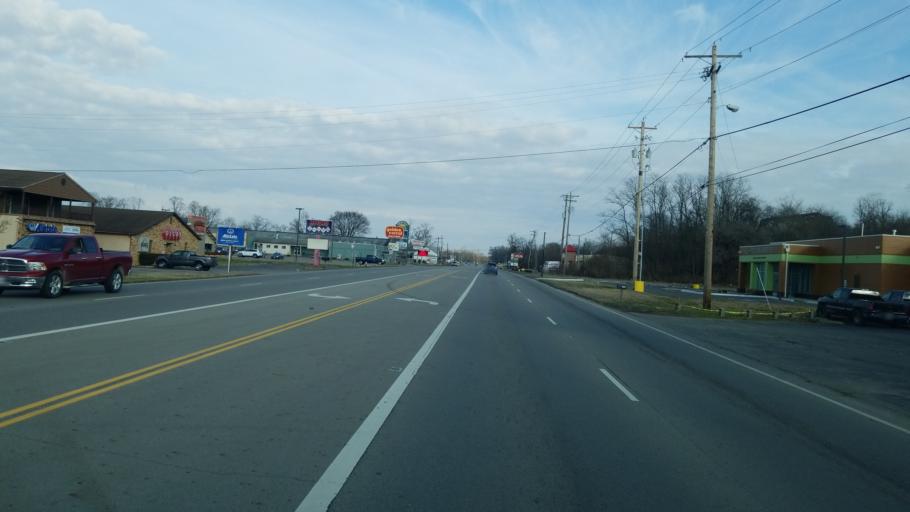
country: US
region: Ohio
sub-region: Ross County
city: Chillicothe
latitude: 39.3685
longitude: -82.9757
